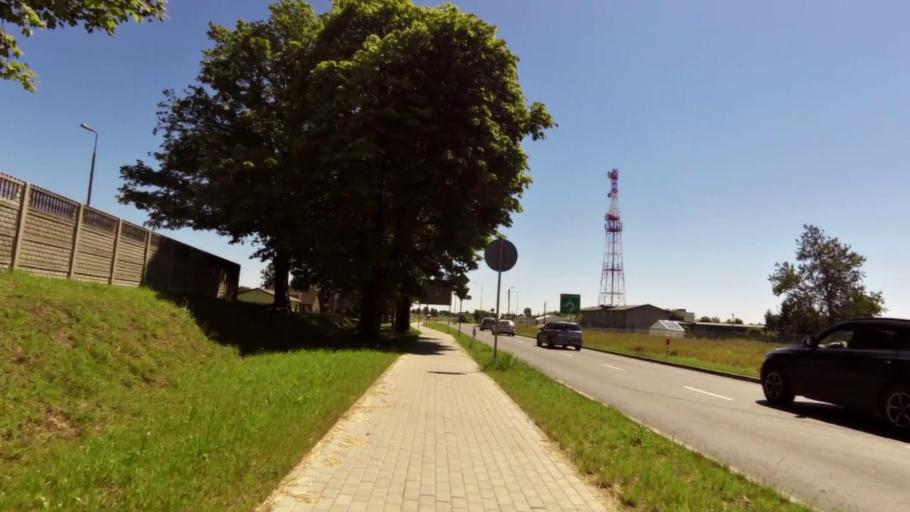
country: PL
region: West Pomeranian Voivodeship
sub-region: Powiat kolobrzeski
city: Goscino
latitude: 54.0550
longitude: 15.6441
